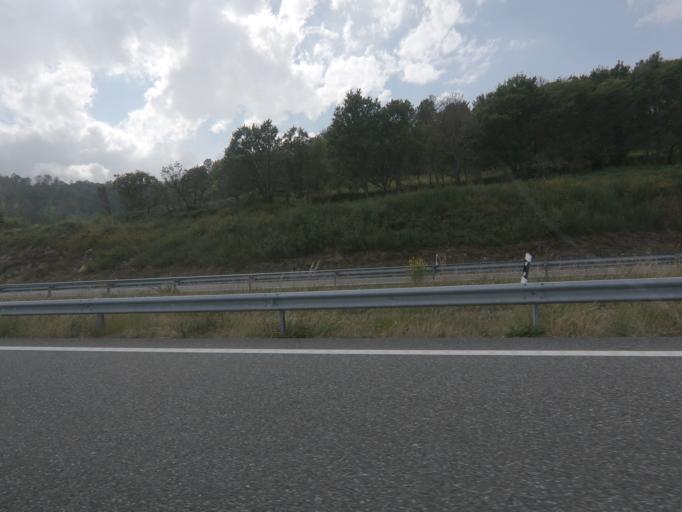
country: ES
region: Galicia
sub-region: Provincia de Ourense
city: Melon
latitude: 42.2518
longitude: -8.2240
